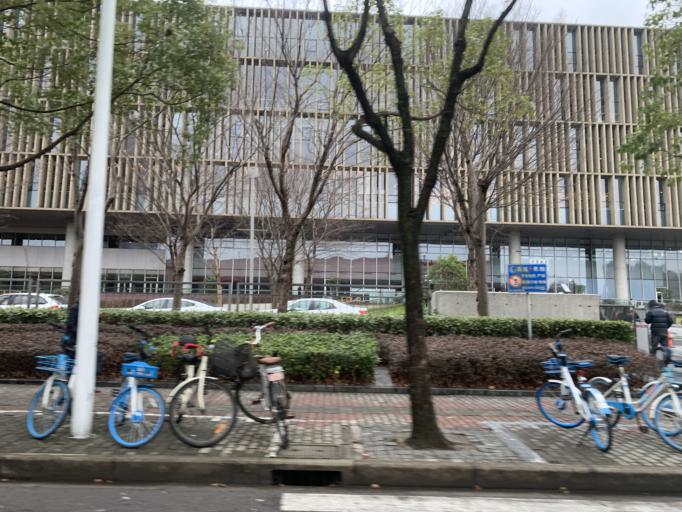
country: CN
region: Shanghai Shi
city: Huamu
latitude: 31.1949
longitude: 121.5369
